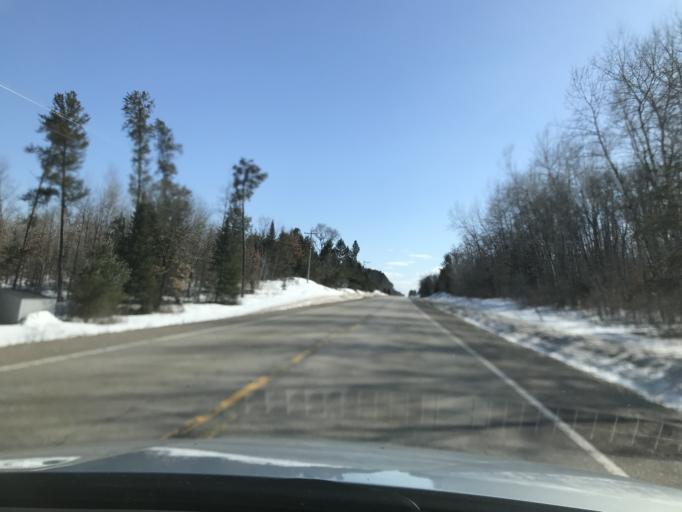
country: US
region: Wisconsin
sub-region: Marinette County
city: Peshtigo
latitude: 45.3305
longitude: -88.1019
